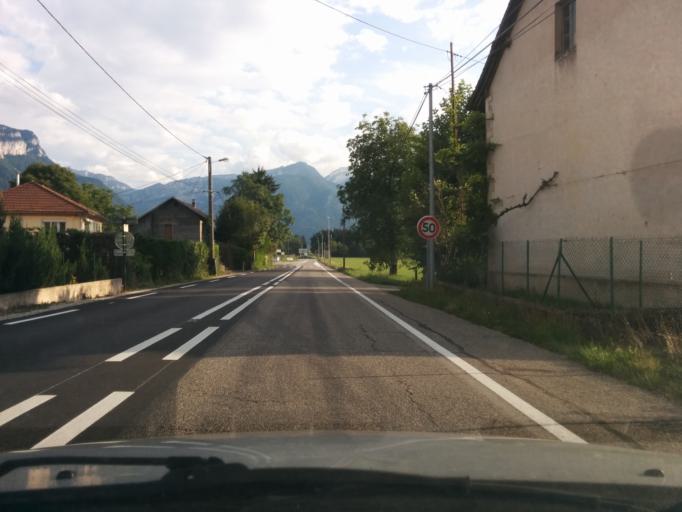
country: FR
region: Rhone-Alpes
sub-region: Departement de l'Isere
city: Entre-deux-Guiers
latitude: 45.4278
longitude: 5.7562
